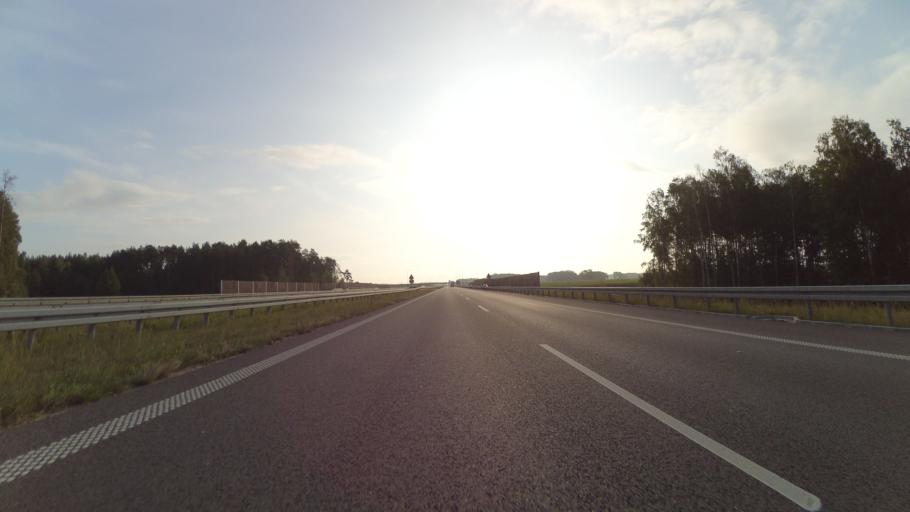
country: PL
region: Podlasie
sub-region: Powiat zambrowski
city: Rutki-Kossaki
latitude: 53.1072
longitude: 22.5705
